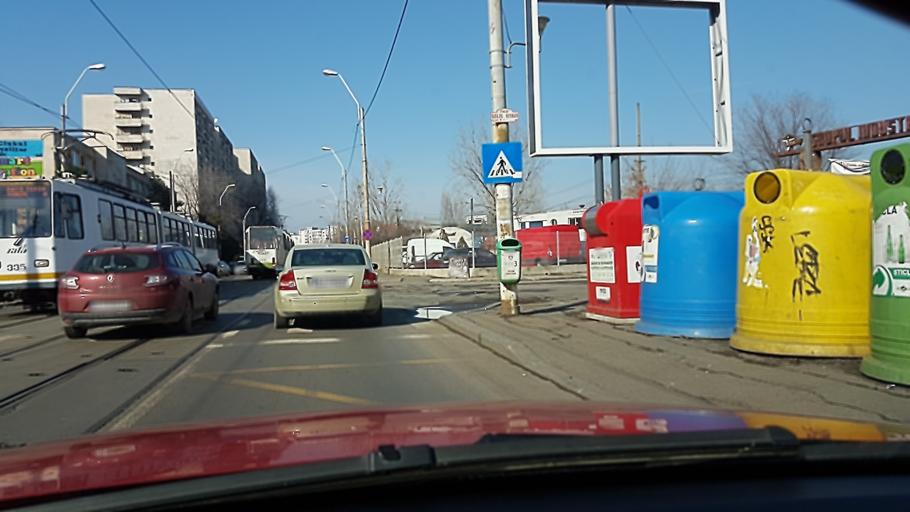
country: RO
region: Ilfov
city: Dobroesti
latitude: 44.4301
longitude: 26.1735
